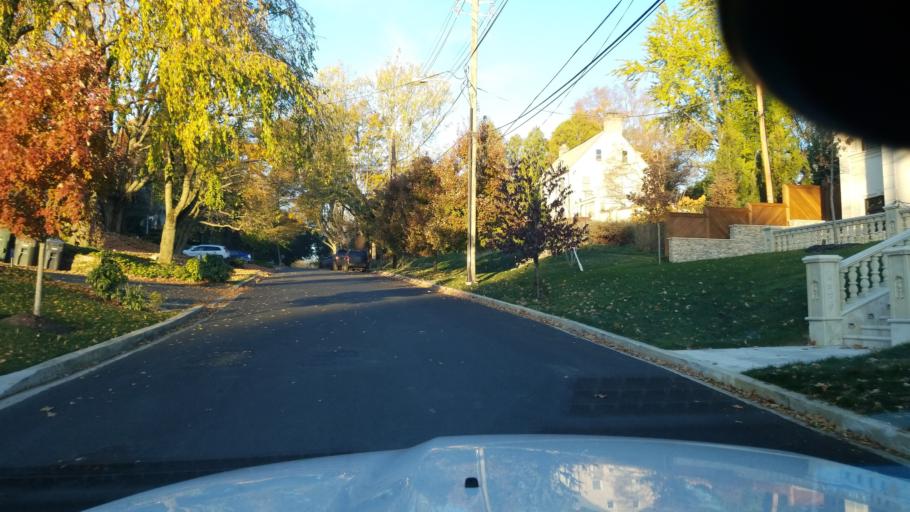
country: US
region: Maryland
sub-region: Montgomery County
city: Chevy Chase Village
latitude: 38.9547
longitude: -77.0660
